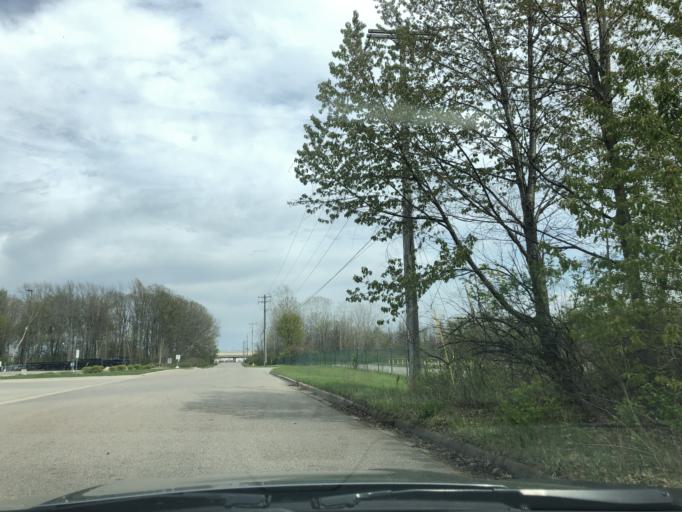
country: US
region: Michigan
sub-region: Eaton County
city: Waverly
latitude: 42.7078
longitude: -84.6470
